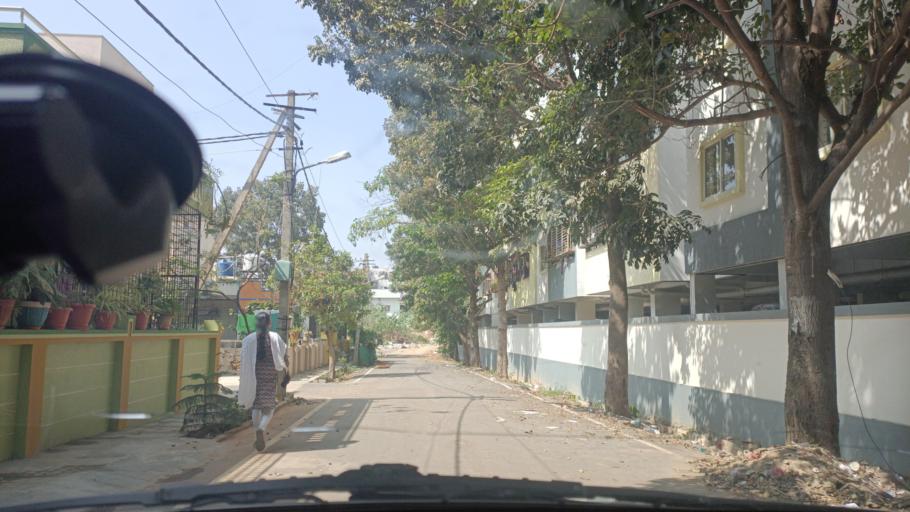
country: IN
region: Karnataka
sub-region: Bangalore Urban
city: Yelahanka
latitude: 13.1189
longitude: 77.6172
